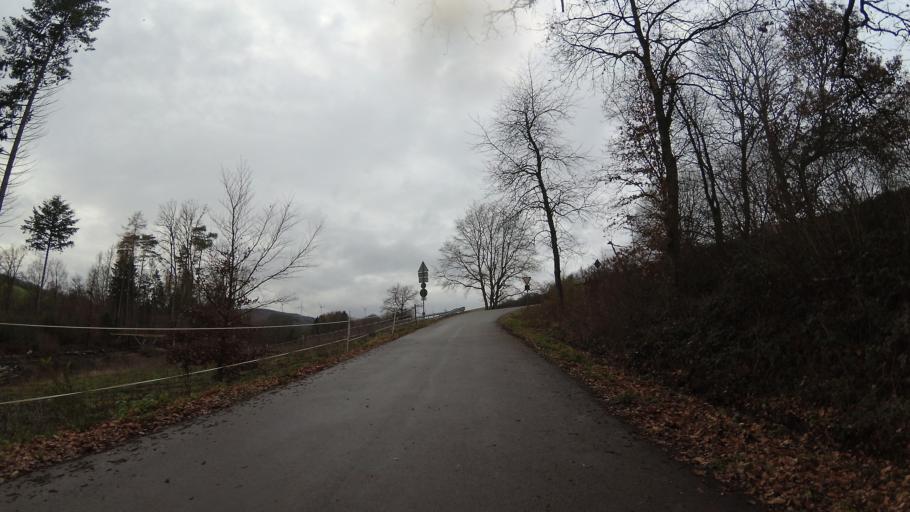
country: DE
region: Rheinland-Pfalz
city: Breitenbach
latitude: 49.4462
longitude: 7.2448
